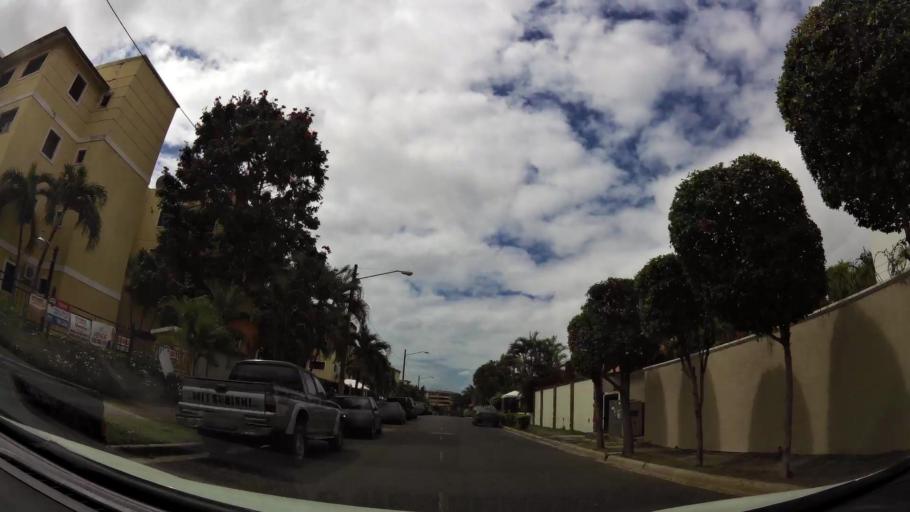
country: DO
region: Nacional
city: Bella Vista
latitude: 18.4670
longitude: -69.9647
